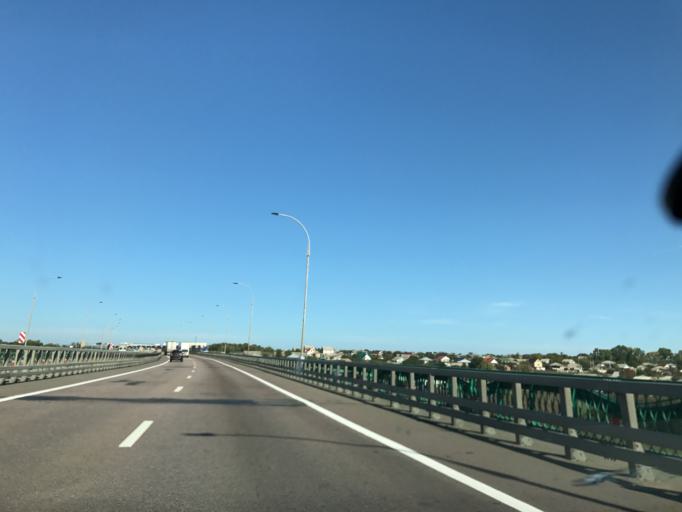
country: RU
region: Voronezj
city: Verkhniy Mamon
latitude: 50.1721
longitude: 40.4288
